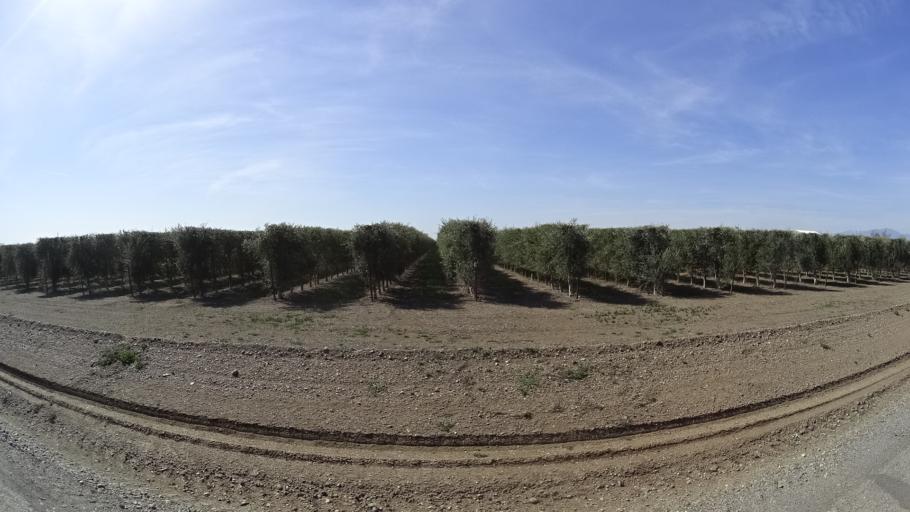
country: US
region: California
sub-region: Glenn County
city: Willows
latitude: 39.6116
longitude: -122.2543
